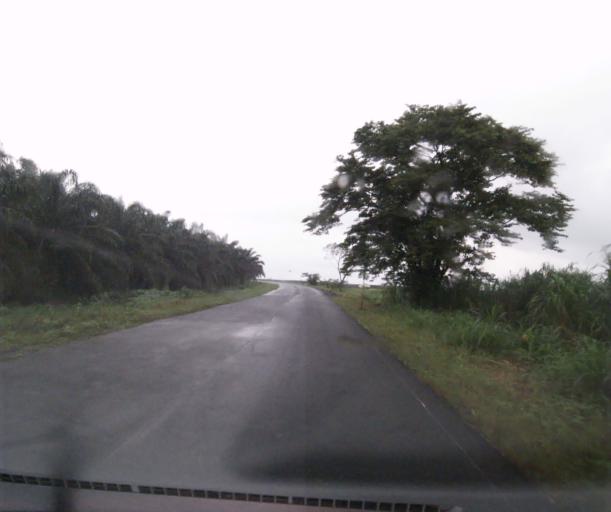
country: CM
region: South-West Province
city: Idenao
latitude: 4.0925
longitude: 8.9911
